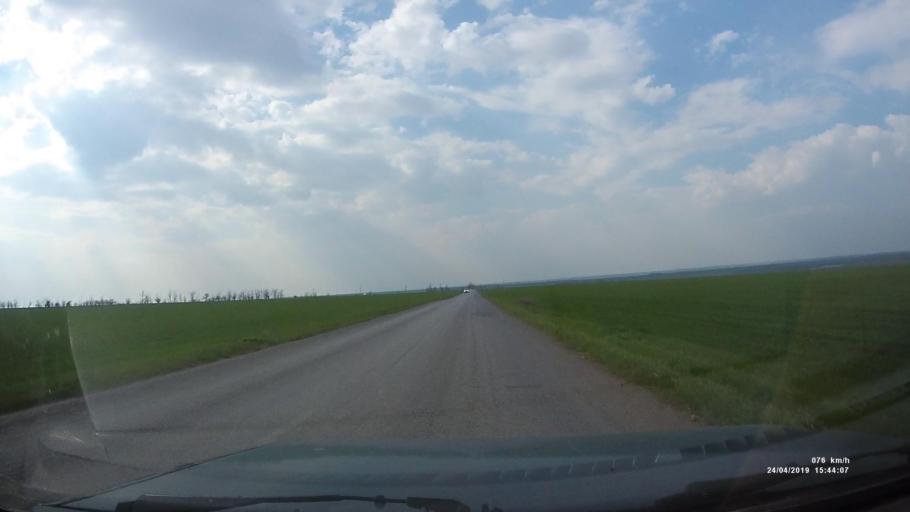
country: RU
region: Kalmykiya
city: Yashalta
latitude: 46.5870
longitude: 42.7621
